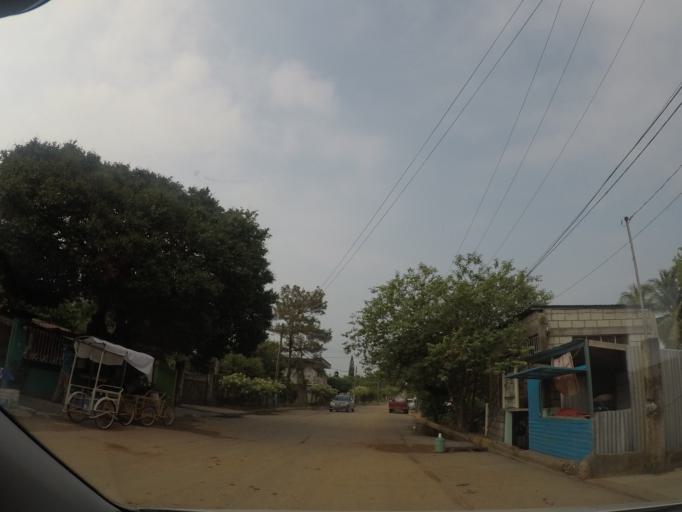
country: MX
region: Oaxaca
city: Matias Romero
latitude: 16.8778
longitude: -95.0473
